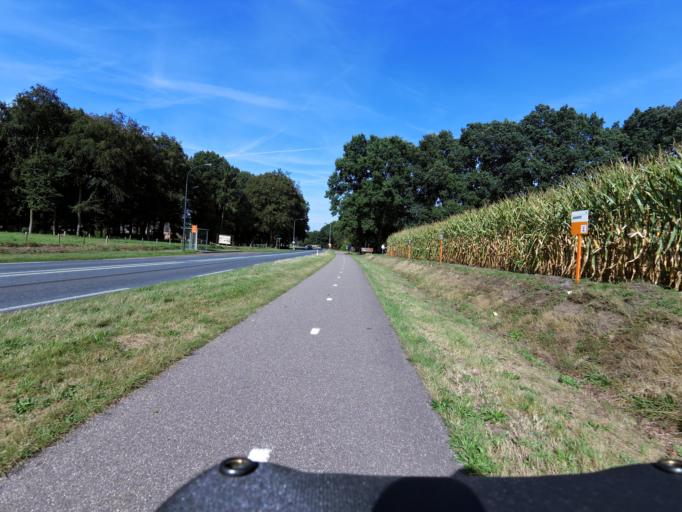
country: NL
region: Gelderland
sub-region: Gemeente Apeldoorn
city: Uddel
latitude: 52.2333
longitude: 5.7714
